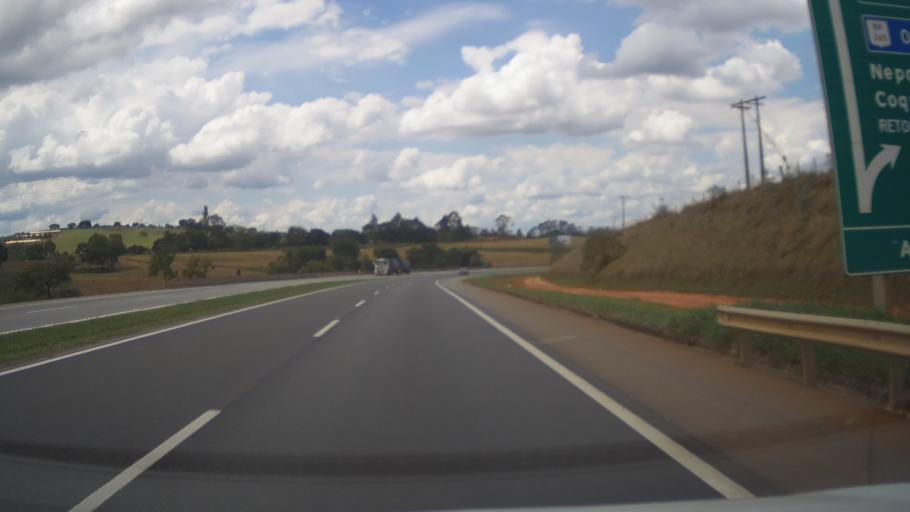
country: BR
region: Minas Gerais
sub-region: Nepomuceno
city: Nepomuceno
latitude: -21.2314
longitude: -45.1342
